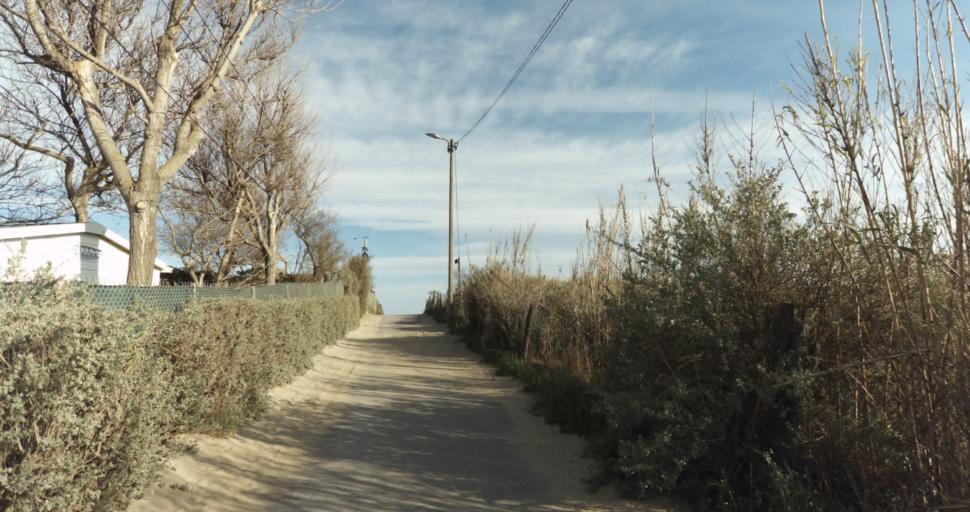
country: FR
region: Languedoc-Roussillon
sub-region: Departement de l'Herault
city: Le Cap d'Agde
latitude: 43.3096
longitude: 3.5461
